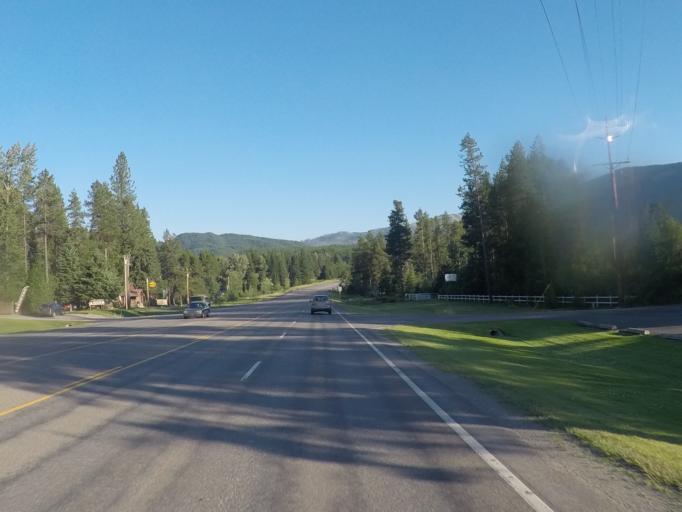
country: US
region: Montana
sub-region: Flathead County
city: Columbia Falls
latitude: 48.3983
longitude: -114.0419
